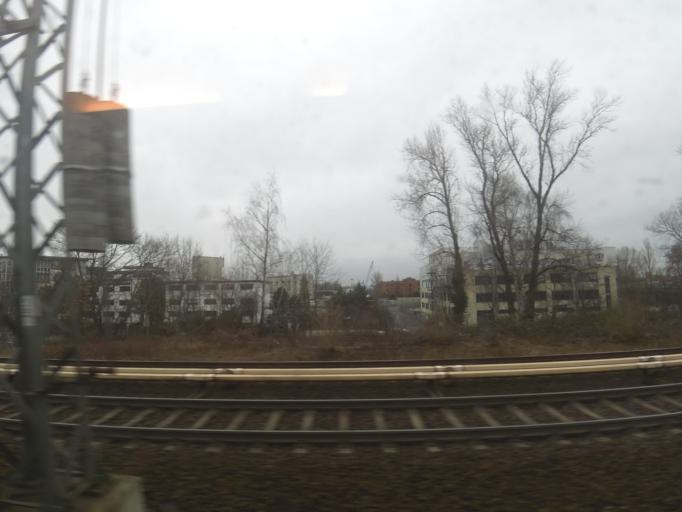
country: DE
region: Berlin
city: Spandau
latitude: 52.5312
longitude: 13.2144
